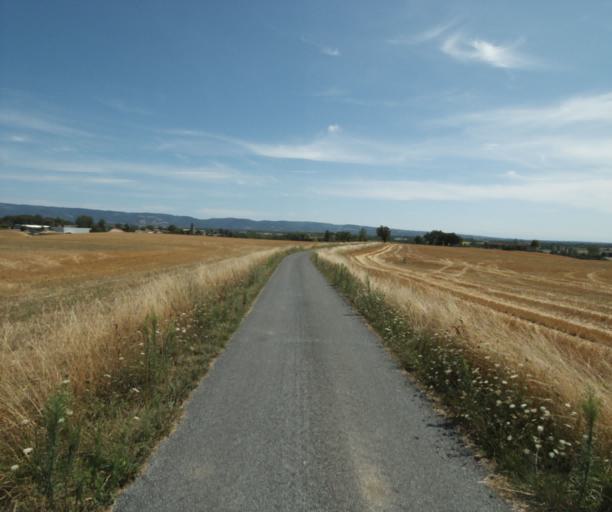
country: FR
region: Midi-Pyrenees
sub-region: Departement du Tarn
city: Puylaurens
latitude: 43.5328
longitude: 2.0029
